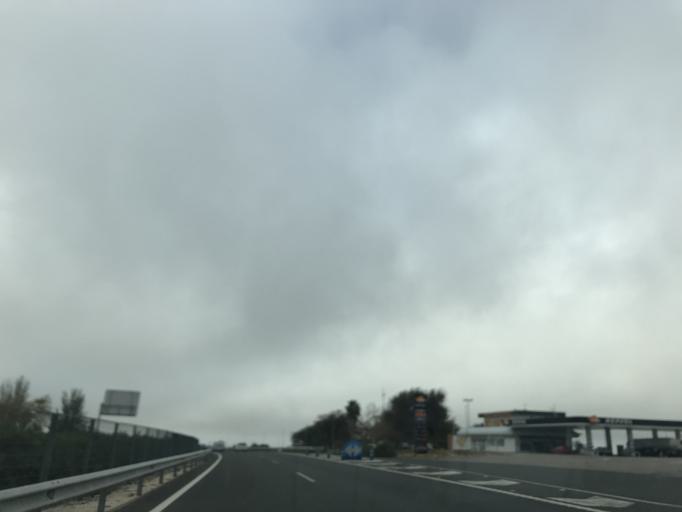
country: ES
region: Andalusia
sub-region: Provincia de Sevilla
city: Estepa
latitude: 37.3024
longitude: -4.8758
